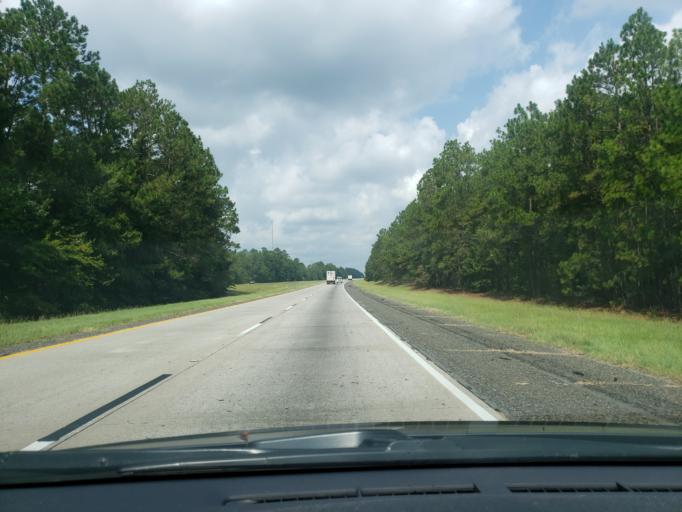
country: US
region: Georgia
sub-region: Treutlen County
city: Soperton
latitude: 32.4355
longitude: -82.6515
